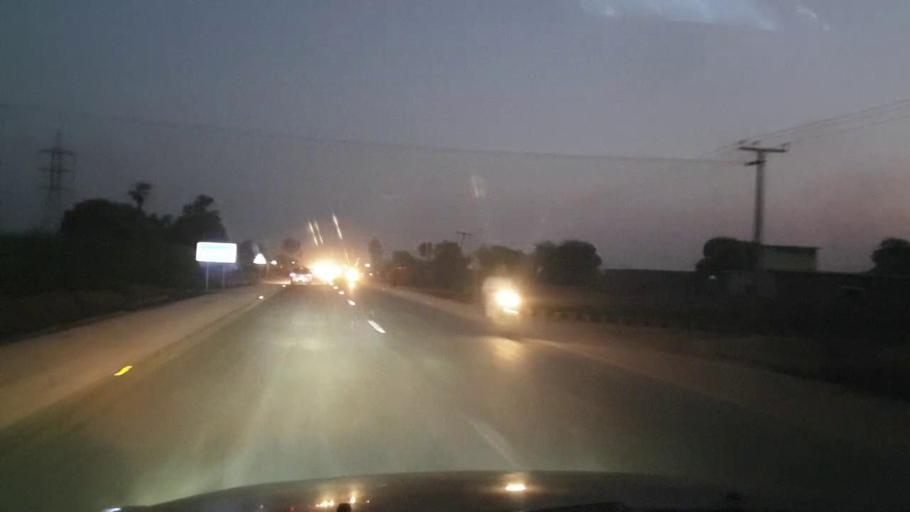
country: PK
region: Sindh
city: Chambar
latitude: 25.3583
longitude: 68.7870
